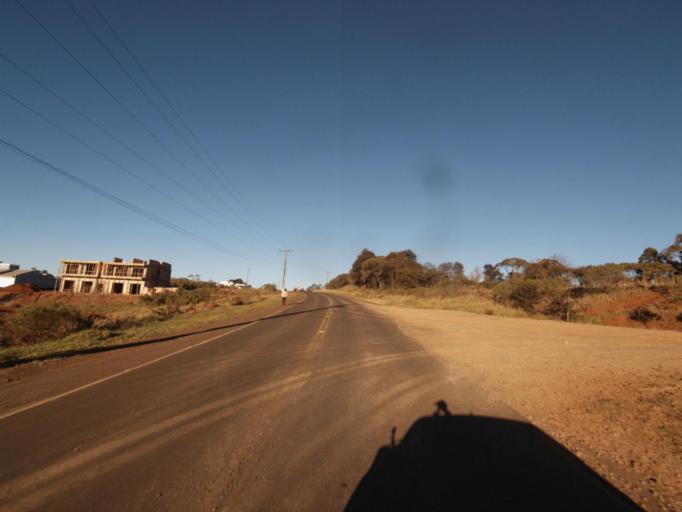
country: AR
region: Misiones
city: Bernardo de Irigoyen
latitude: -26.2695
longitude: -53.6342
